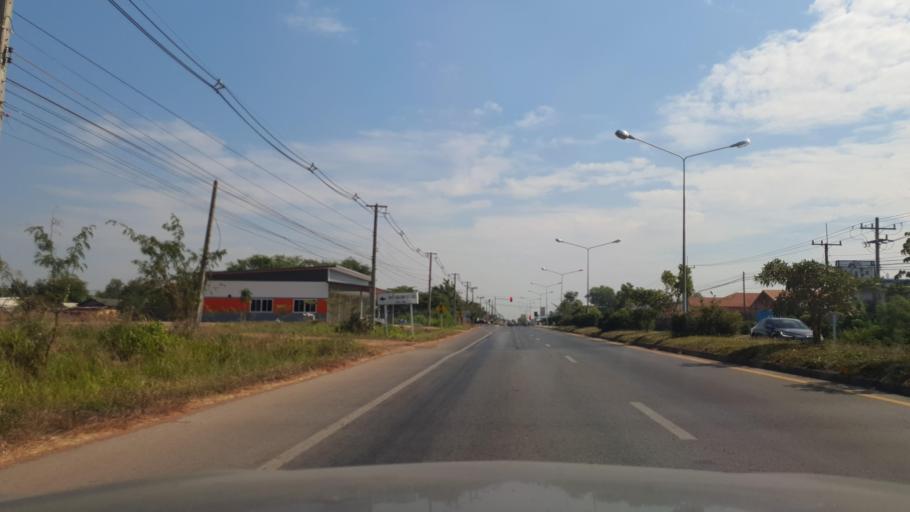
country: TH
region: Maha Sarakham
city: Kantharawichai
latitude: 16.3939
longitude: 103.2967
